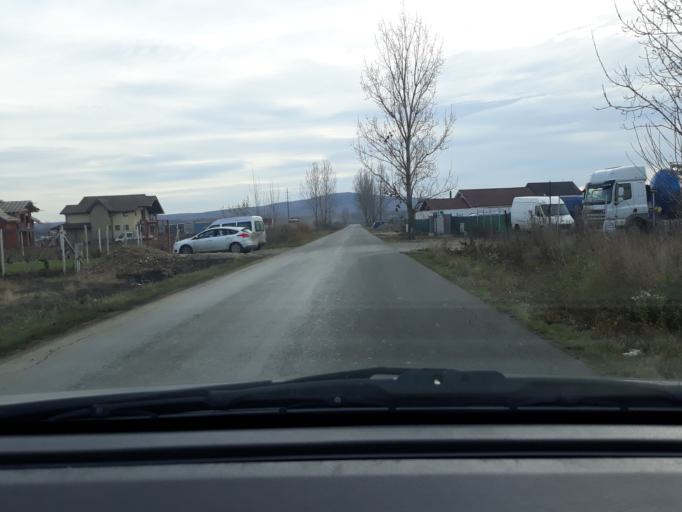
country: RO
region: Bihor
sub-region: Comuna Sanmartin
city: Sanmartin
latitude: 47.0243
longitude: 22.0041
